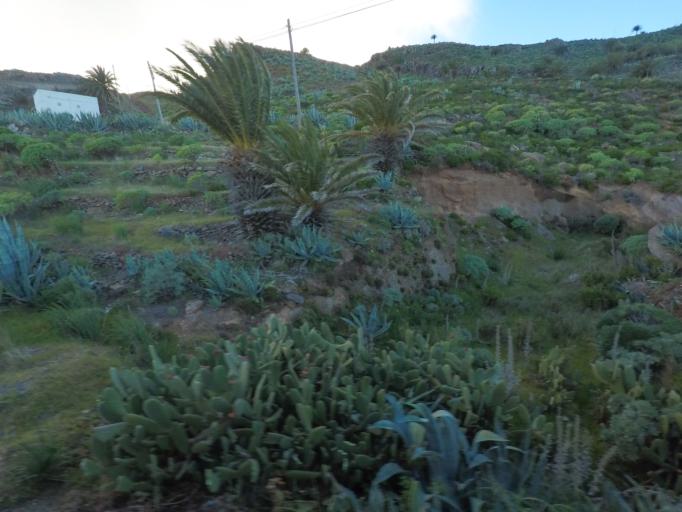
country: ES
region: Canary Islands
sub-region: Provincia de Santa Cruz de Tenerife
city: San Sebastian de la Gomera
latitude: 28.0998
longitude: -17.1717
